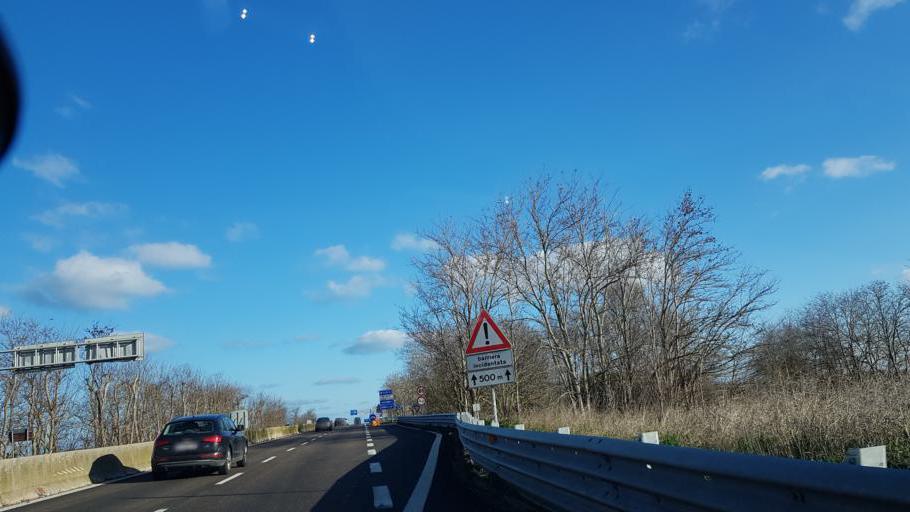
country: IT
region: Apulia
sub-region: Provincia di Brindisi
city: La Rosa
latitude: 40.6181
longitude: 17.9482
